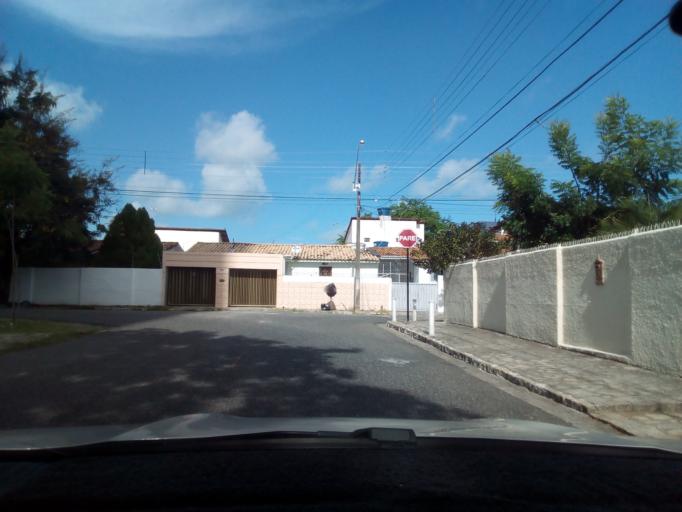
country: BR
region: Paraiba
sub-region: Joao Pessoa
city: Joao Pessoa
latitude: -7.1107
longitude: -34.8402
